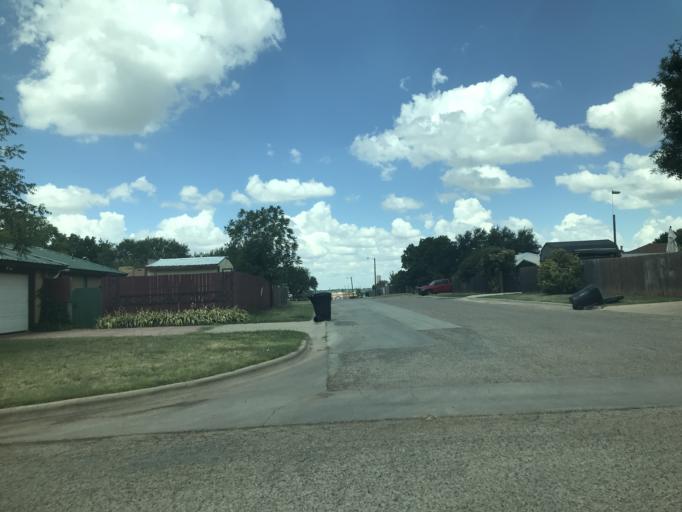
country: US
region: Texas
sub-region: Taylor County
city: Abilene
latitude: 32.4417
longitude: -99.7024
